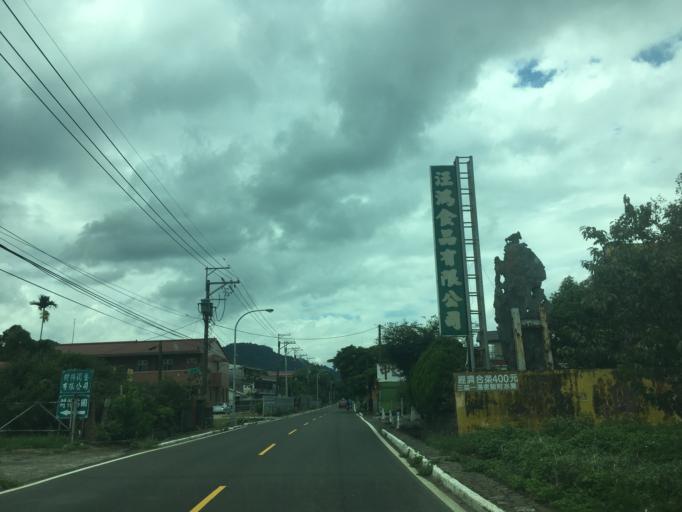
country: TW
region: Taiwan
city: Daxi
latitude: 24.8534
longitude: 121.2903
